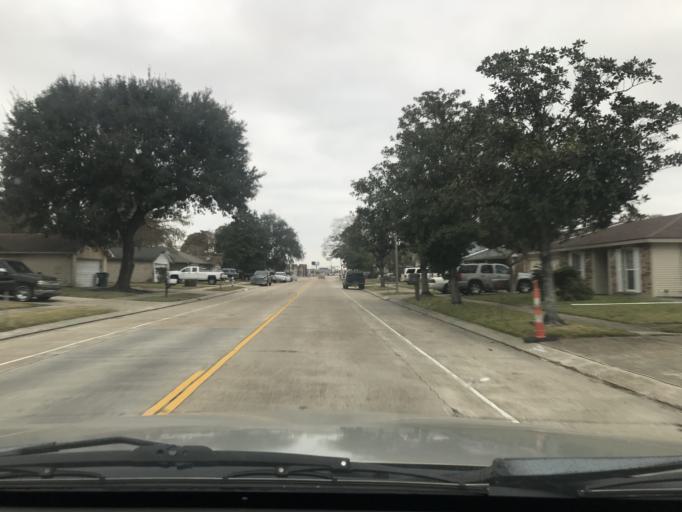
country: US
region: Louisiana
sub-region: Jefferson Parish
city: Woodmere
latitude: 29.8658
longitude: -90.0807
